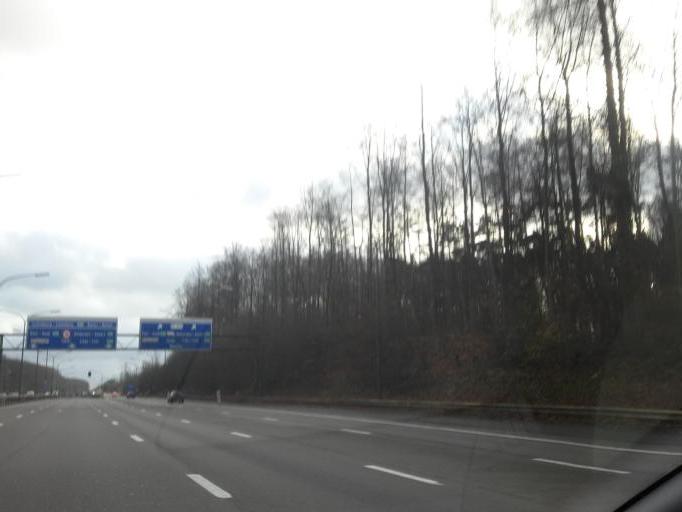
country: BE
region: Flanders
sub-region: Provincie Vlaams-Brabant
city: Hoeilaart
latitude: 50.8031
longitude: 4.4597
